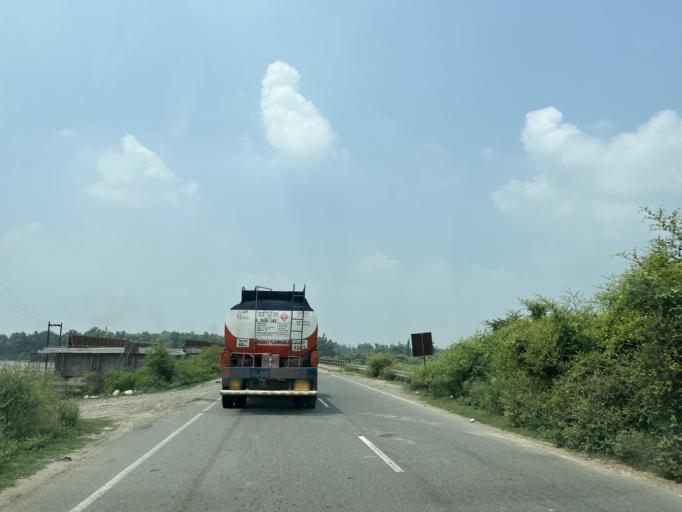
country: IN
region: Uttarakhand
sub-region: Haridwar
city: Haridwar
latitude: 29.8397
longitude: 78.1941
